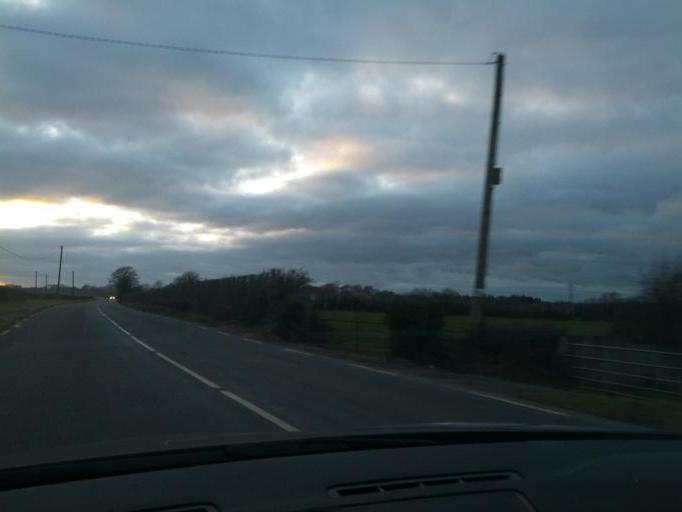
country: IE
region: Leinster
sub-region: Uibh Fhaili
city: Banagher
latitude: 53.1062
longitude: -8.0320
